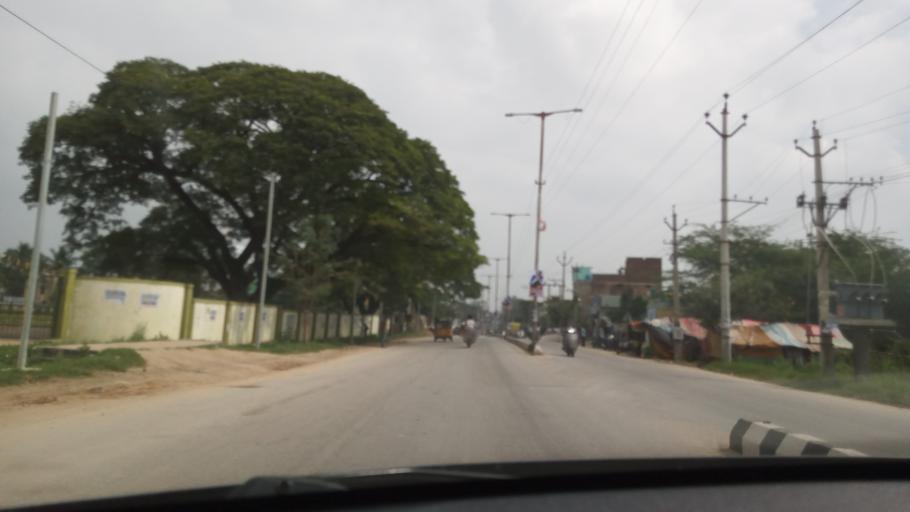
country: IN
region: Andhra Pradesh
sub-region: Chittoor
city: Madanapalle
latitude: 13.5560
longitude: 78.4953
